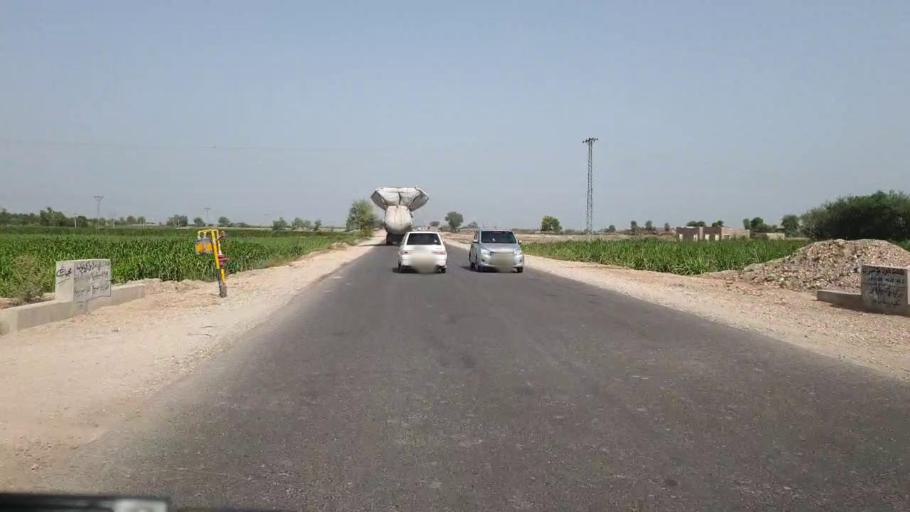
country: PK
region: Sindh
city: Sakrand
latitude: 26.2678
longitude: 68.1684
